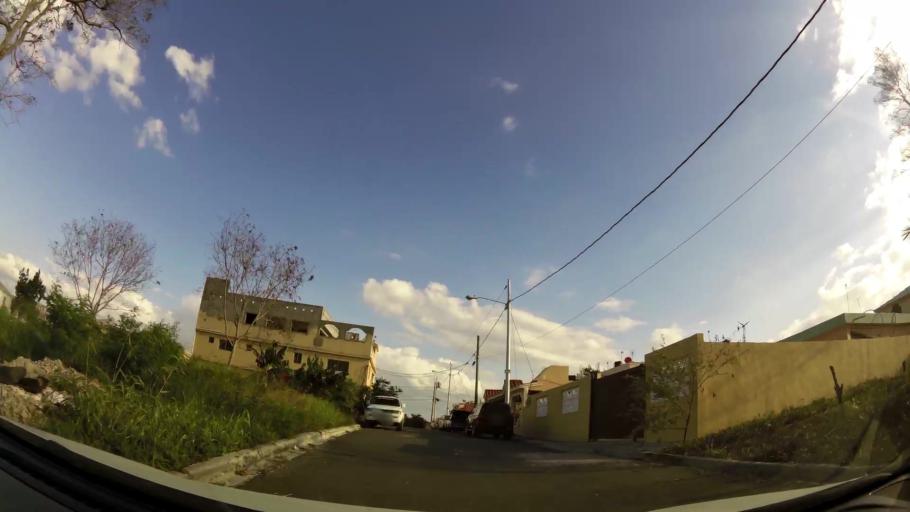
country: DO
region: Nacional
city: Ensanche Luperon
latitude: 18.5483
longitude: -69.9157
